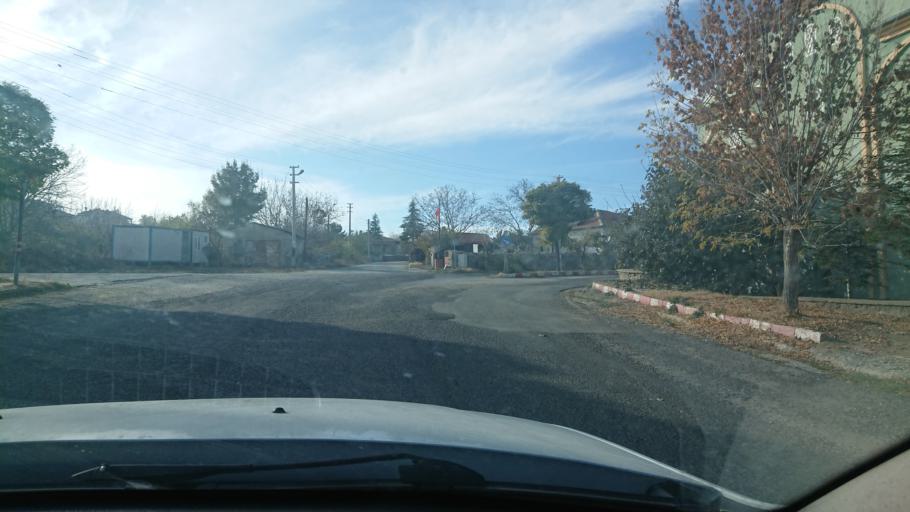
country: TR
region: Aksaray
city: Sariyahsi
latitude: 38.9606
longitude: 33.8812
